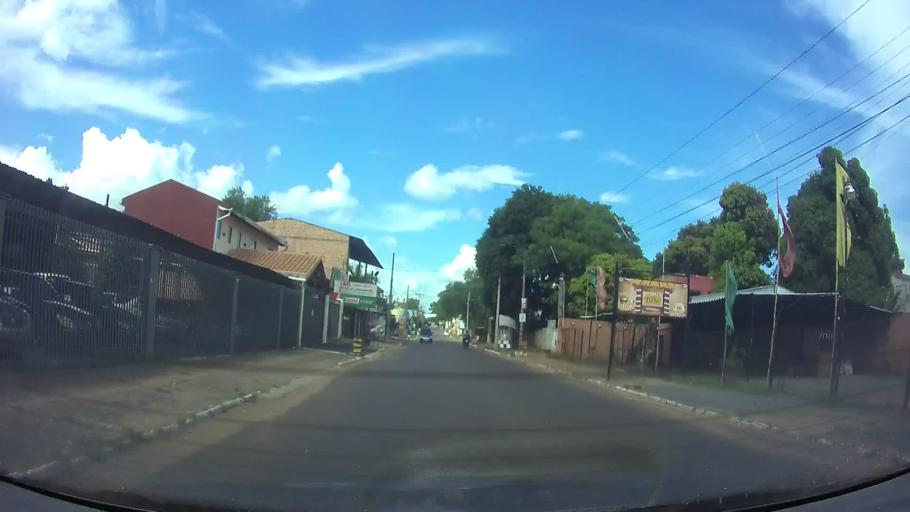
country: PY
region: Central
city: Villa Elisa
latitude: -25.3417
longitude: -57.5751
